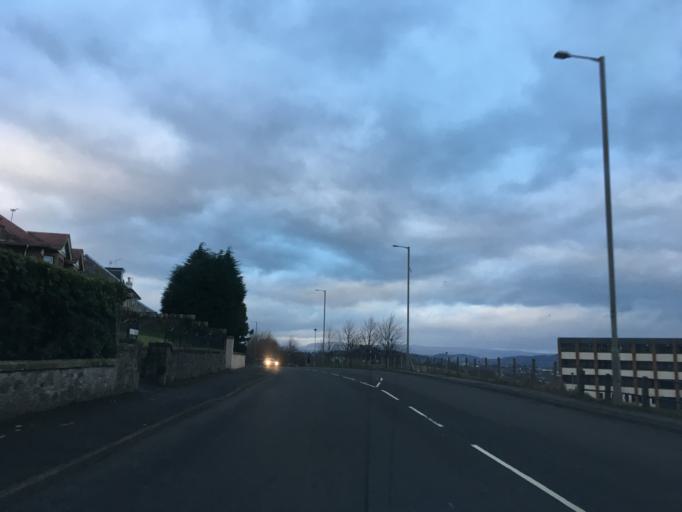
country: GB
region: Scotland
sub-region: Stirling
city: Bannockburn
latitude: 56.0948
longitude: -3.9220
